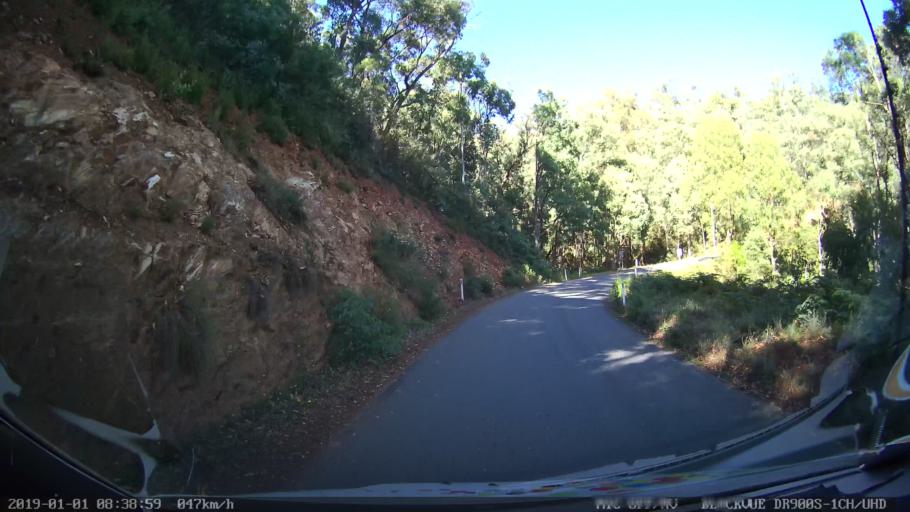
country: AU
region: New South Wales
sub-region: Snowy River
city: Jindabyne
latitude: -36.3333
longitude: 148.1946
